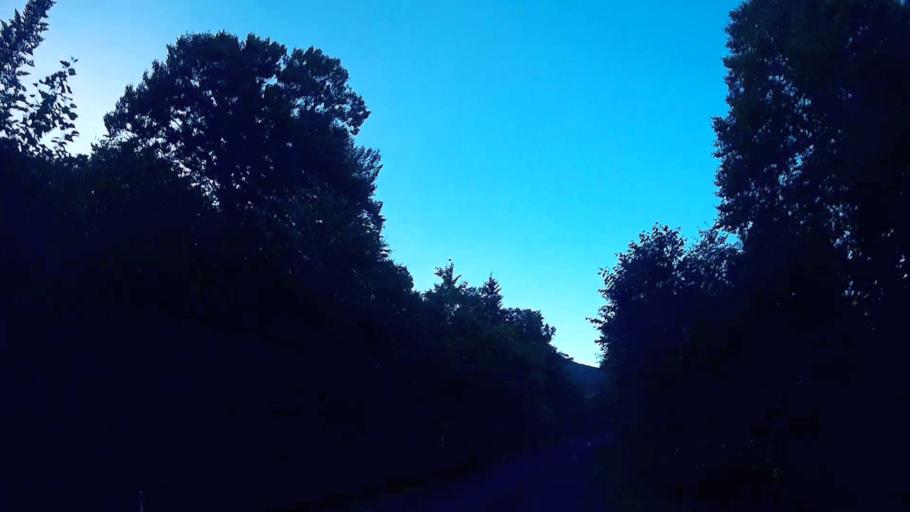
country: JP
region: Hokkaido
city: Iwanai
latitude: 42.6000
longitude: 139.9903
